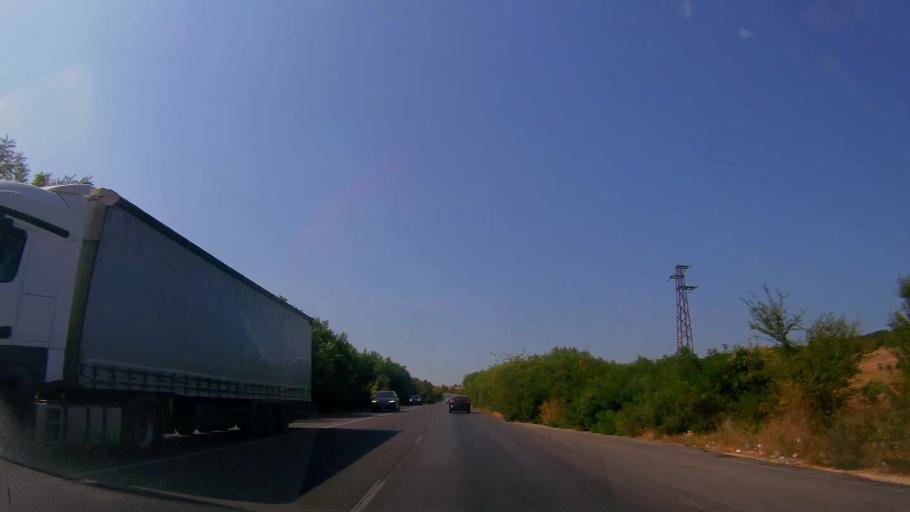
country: BG
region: Ruse
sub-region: Obshtina Vetovo
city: Senovo
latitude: 43.5607
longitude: 26.3854
